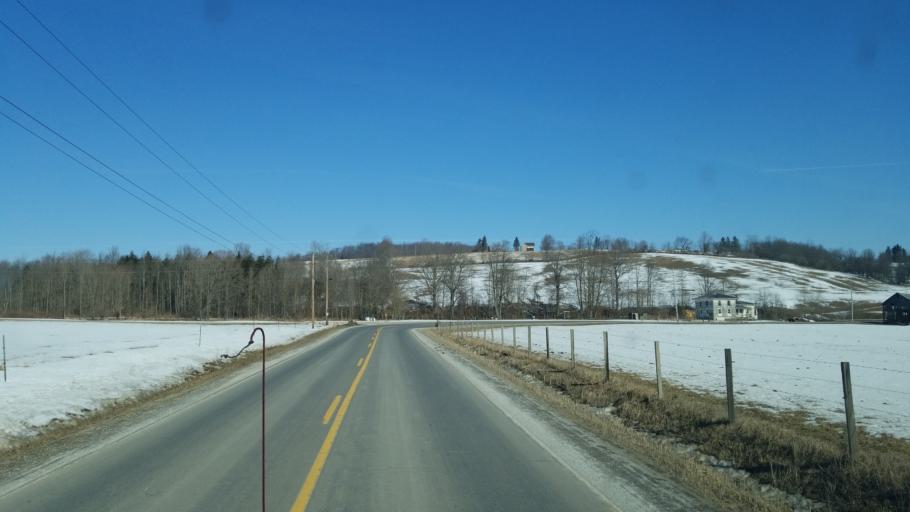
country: US
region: Pennsylvania
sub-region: Tioga County
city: Elkland
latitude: 42.0741
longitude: -77.4301
